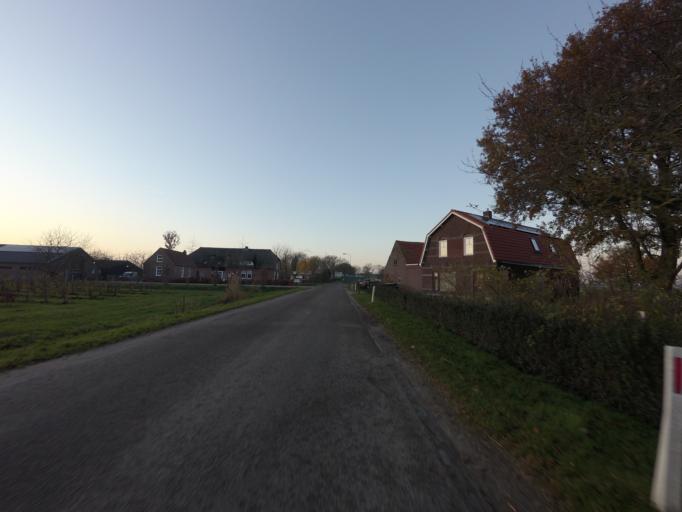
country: NL
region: Gelderland
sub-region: Gemeente Maasdriel
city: Hedel
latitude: 51.7600
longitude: 5.2272
